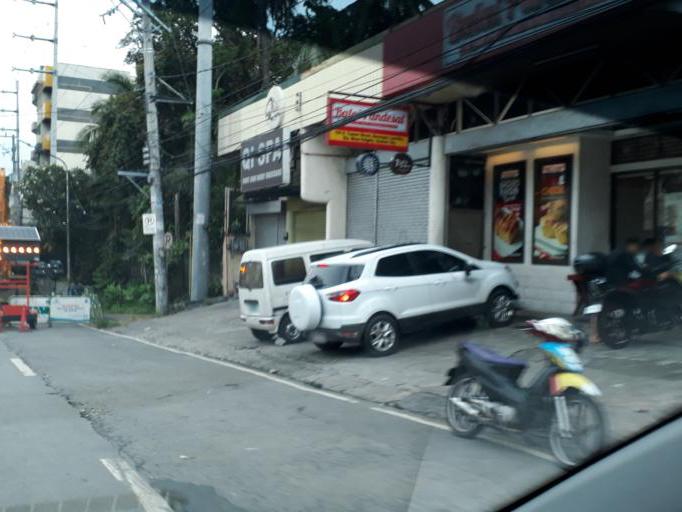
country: PH
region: Calabarzon
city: Del Monte
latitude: 14.6251
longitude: 121.0020
